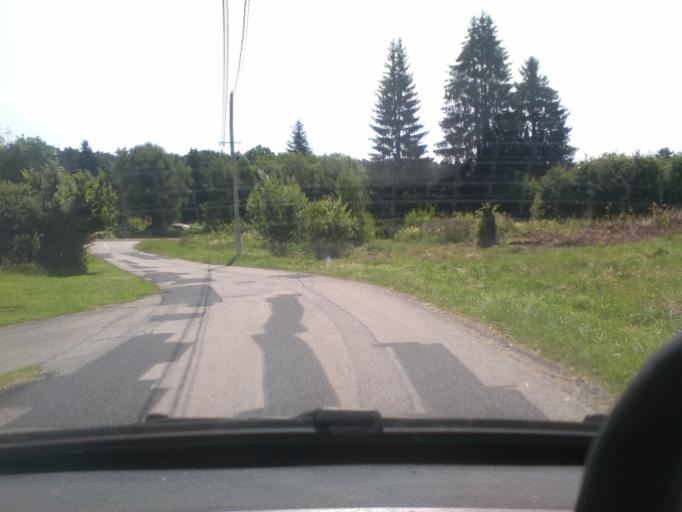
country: FR
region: Lorraine
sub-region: Departement des Vosges
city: Sainte-Marguerite
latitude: 48.2863
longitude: 6.9867
